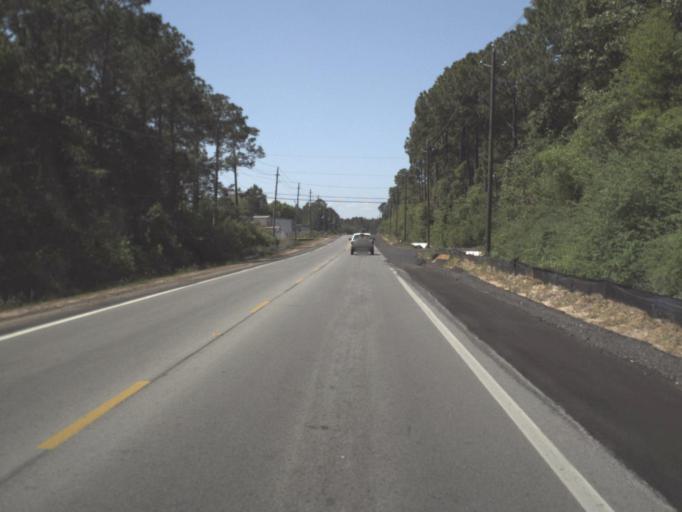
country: US
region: Florida
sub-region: Escambia County
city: Myrtle Grove
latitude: 30.3910
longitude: -87.3102
